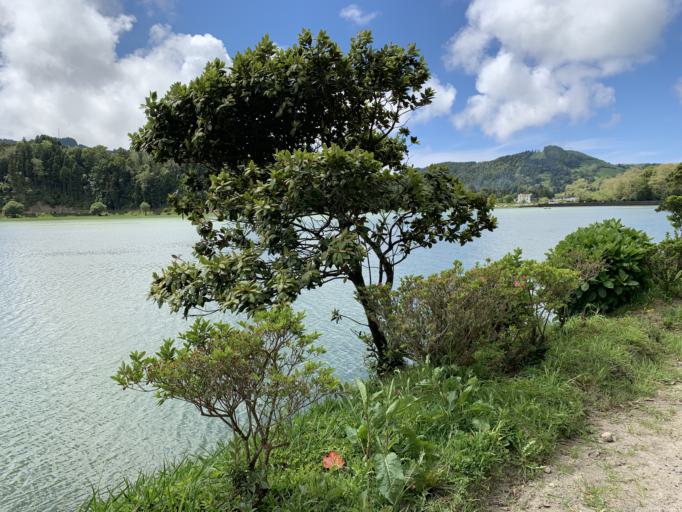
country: PT
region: Azores
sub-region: Ponta Delgada
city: Arrifes
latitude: 37.8516
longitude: -25.7857
